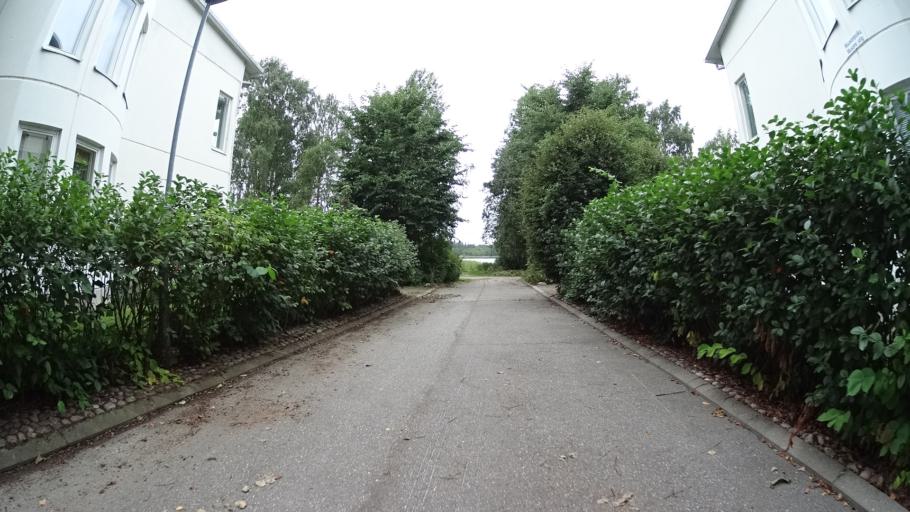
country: FI
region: Uusimaa
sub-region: Helsinki
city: Teekkarikylae
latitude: 60.2074
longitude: 24.8533
